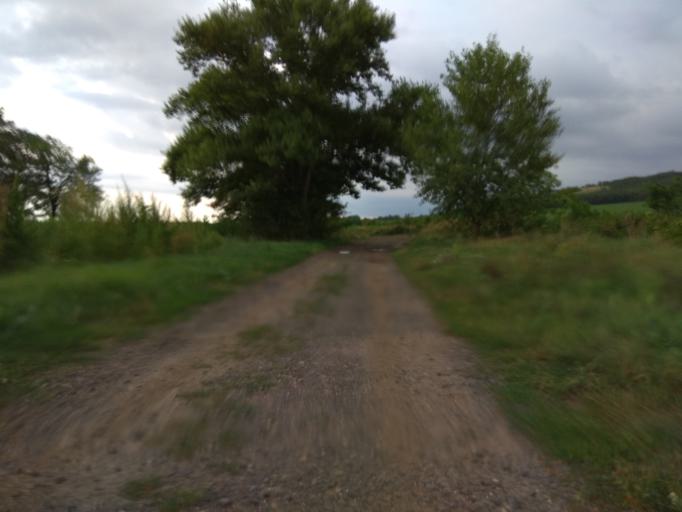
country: HU
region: Borsod-Abauj-Zemplen
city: Monok
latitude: 48.1729
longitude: 21.1199
